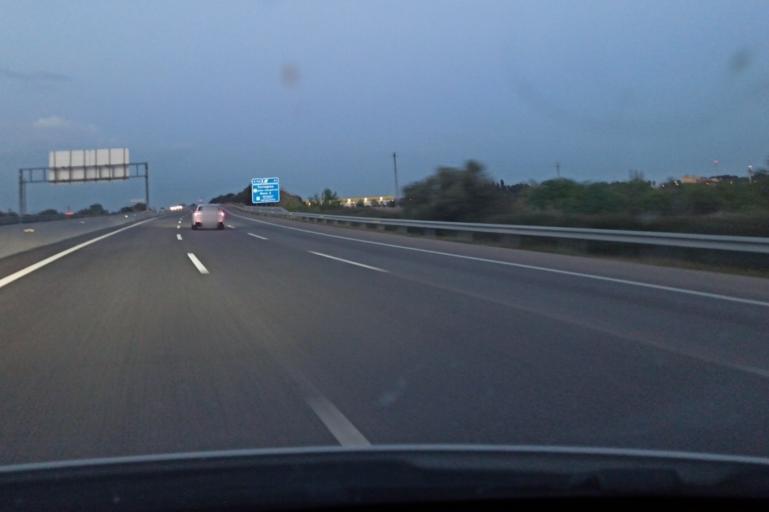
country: ES
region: Catalonia
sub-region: Provincia de Tarragona
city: Vila-seca
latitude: 41.1167
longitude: 1.1377
